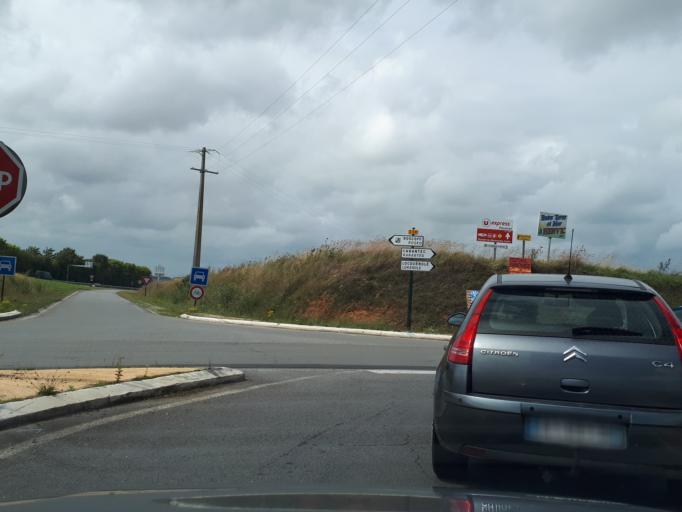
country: FR
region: Brittany
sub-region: Departement du Finistere
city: Henvic
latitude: 48.6368
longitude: -3.9245
